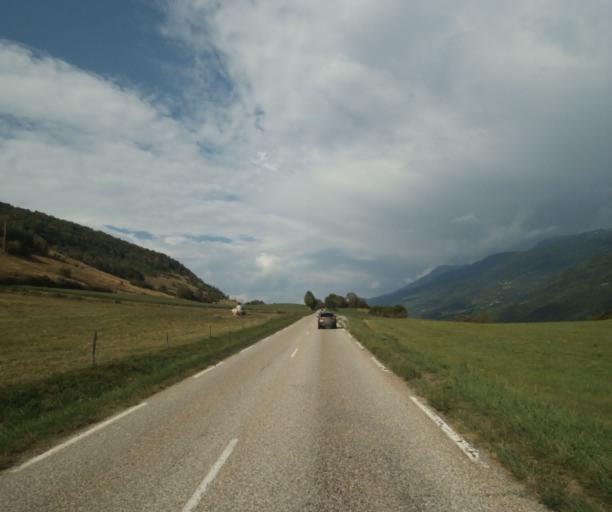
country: FR
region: Rhone-Alpes
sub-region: Departement de l'Isere
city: Vizille
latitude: 45.0945
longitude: 5.7821
